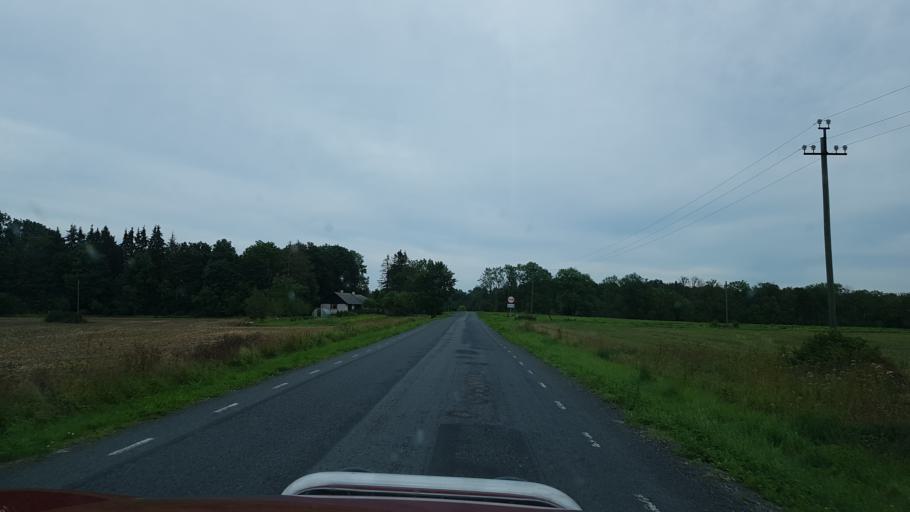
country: EE
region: Laeaene
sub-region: Lihula vald
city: Lihula
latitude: 58.8760
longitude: 23.8662
